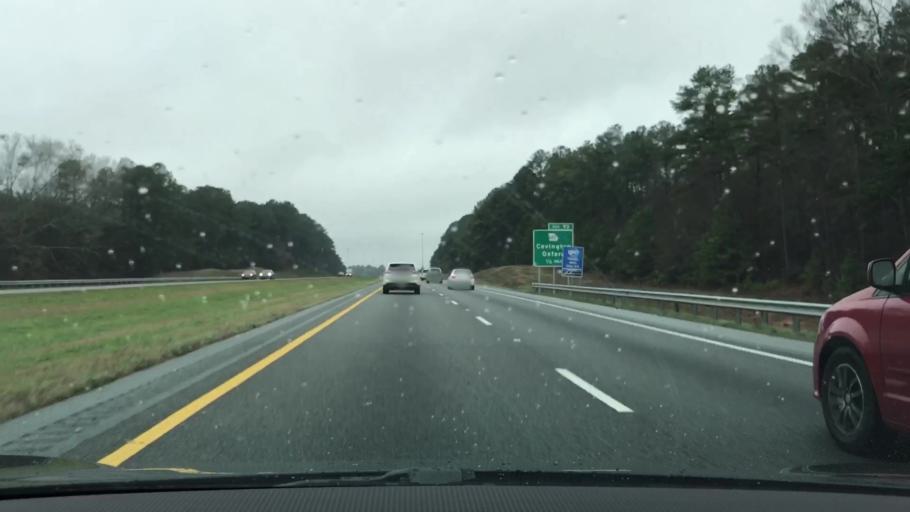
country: US
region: Georgia
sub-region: Newton County
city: Covington
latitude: 33.6114
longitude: -83.8116
